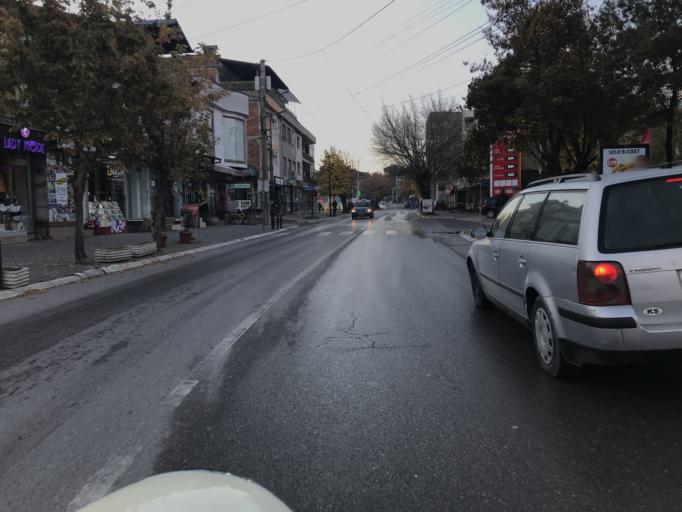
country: XK
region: Pec
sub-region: Komuna e Pejes
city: Peje
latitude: 42.6592
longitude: 20.2928
